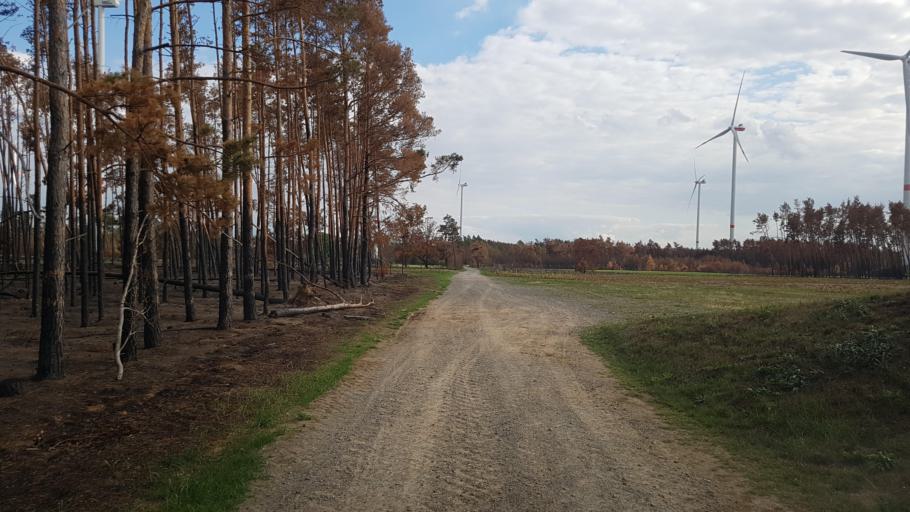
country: DE
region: Saxony
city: Arzberg
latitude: 51.5696
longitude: 13.1792
